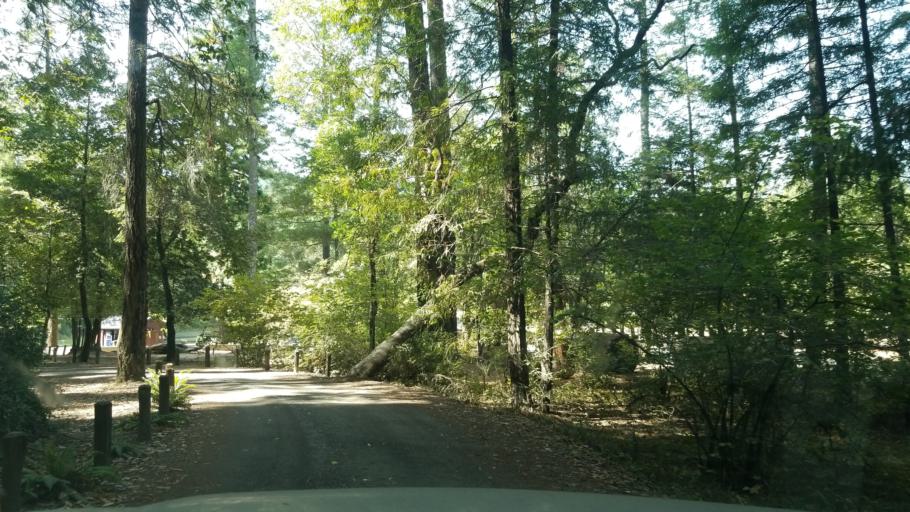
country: US
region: California
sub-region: Humboldt County
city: Redway
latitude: 39.8587
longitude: -123.7186
